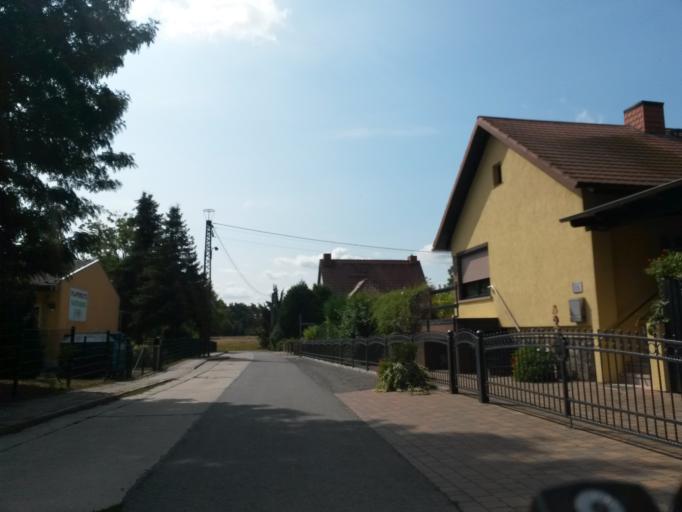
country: DE
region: Saxony-Anhalt
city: Muhlanger
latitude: 51.8144
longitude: 12.7719
